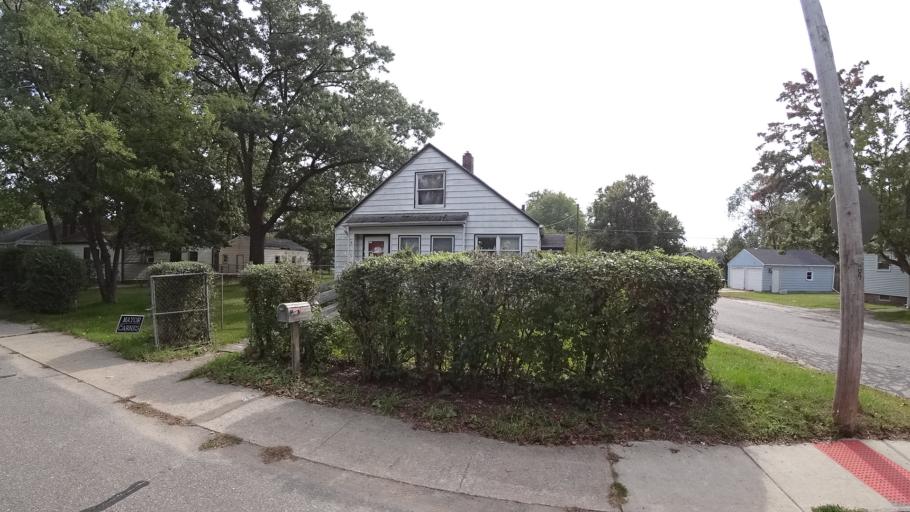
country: US
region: Indiana
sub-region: LaPorte County
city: Trail Creek
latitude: 41.7168
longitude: -86.8672
